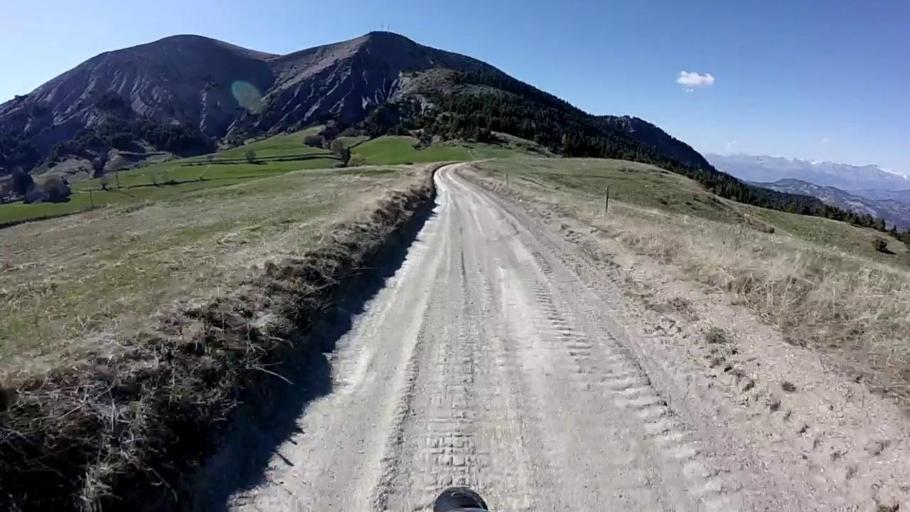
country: FR
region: Provence-Alpes-Cote d'Azur
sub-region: Departement des Alpes-de-Haute-Provence
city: Seyne-les-Alpes
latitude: 44.3288
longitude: 6.3064
